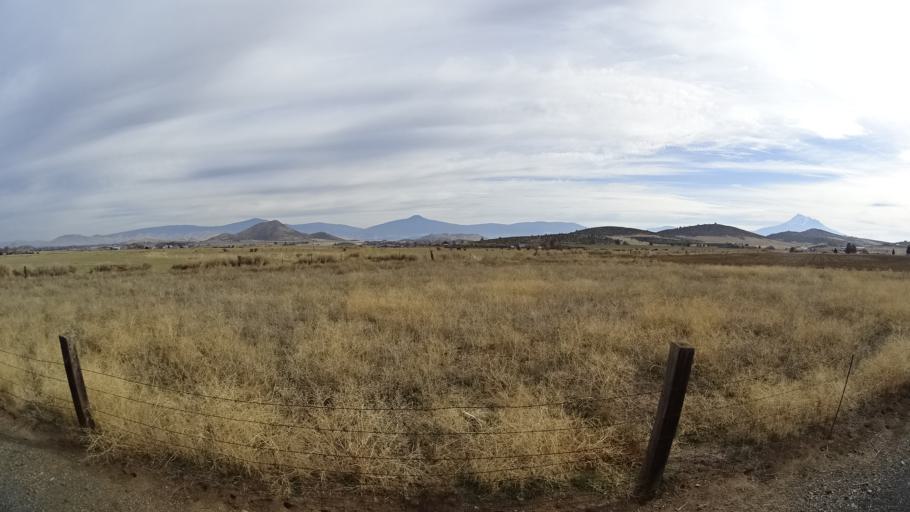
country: US
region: California
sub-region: Siskiyou County
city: Montague
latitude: 41.6986
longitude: -122.5639
